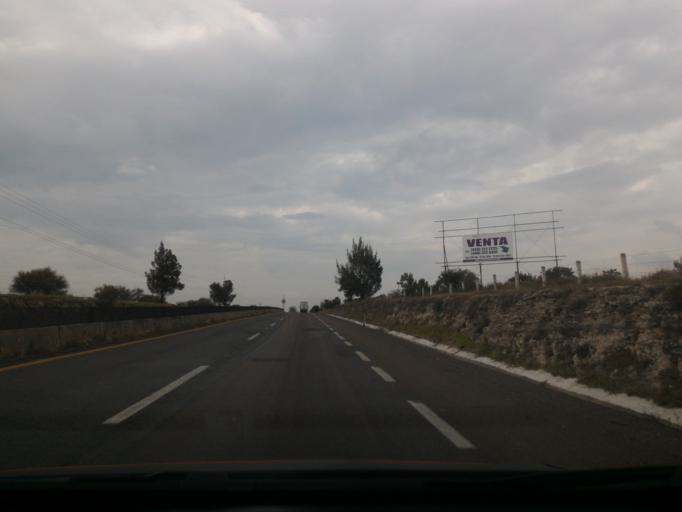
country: MX
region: Aguascalientes
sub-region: Aguascalientes
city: Penuelas (El Cienegal)
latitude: 21.6540
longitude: -102.2822
